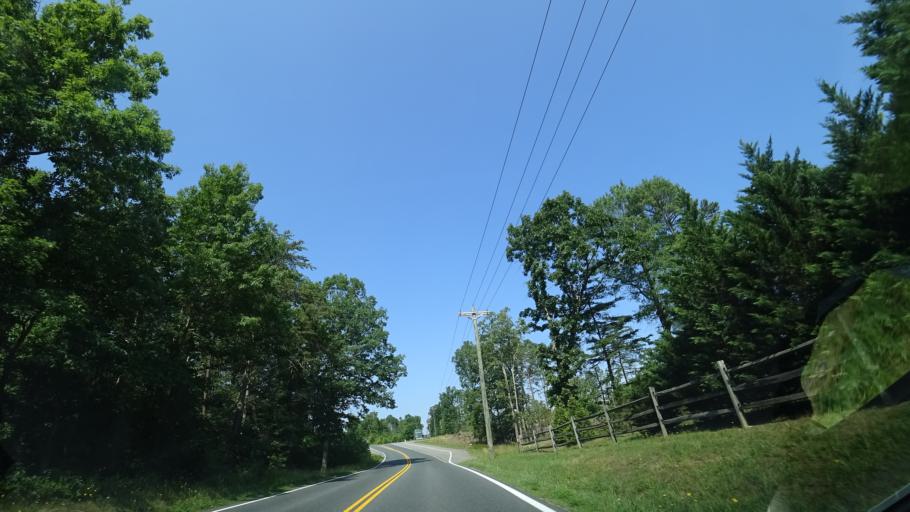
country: US
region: Virginia
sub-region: Louisa County
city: Louisa
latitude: 38.0842
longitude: -77.8451
